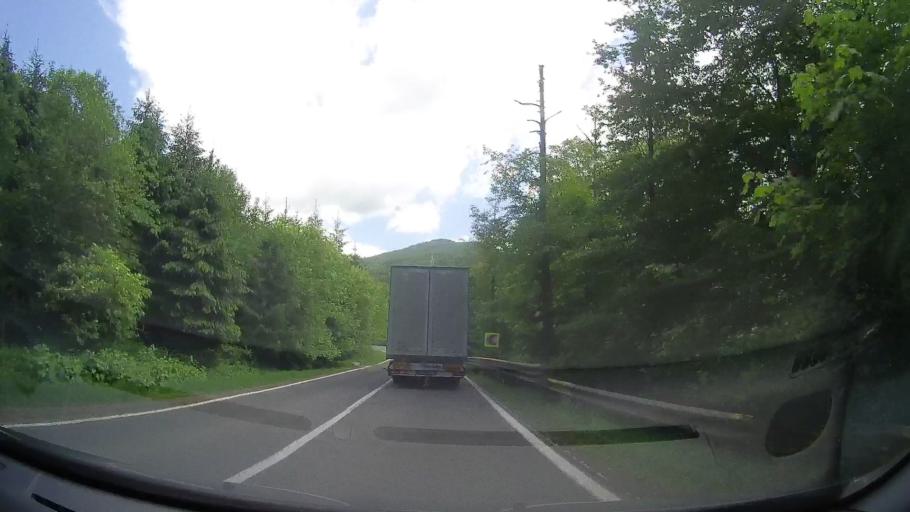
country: RO
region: Prahova
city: Maneciu
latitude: 45.3695
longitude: 25.9298
